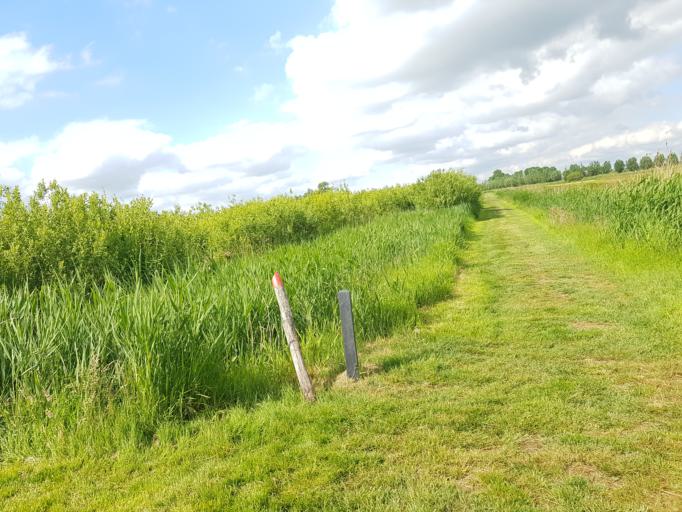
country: NL
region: Friesland
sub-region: Gemeente Smallingerland
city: Oudega
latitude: 53.0923
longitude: 5.9554
